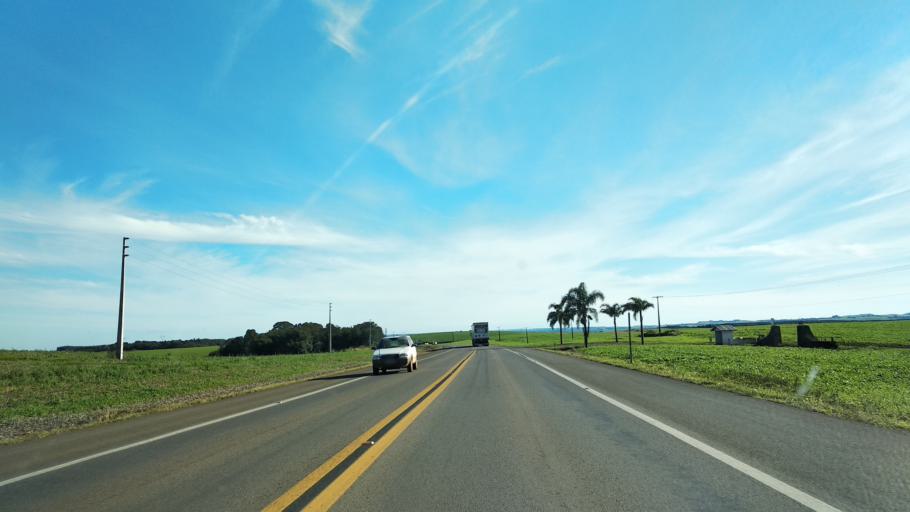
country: BR
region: Santa Catarina
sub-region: Campos Novos
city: Campos Novos
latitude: -27.4904
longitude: -51.3295
